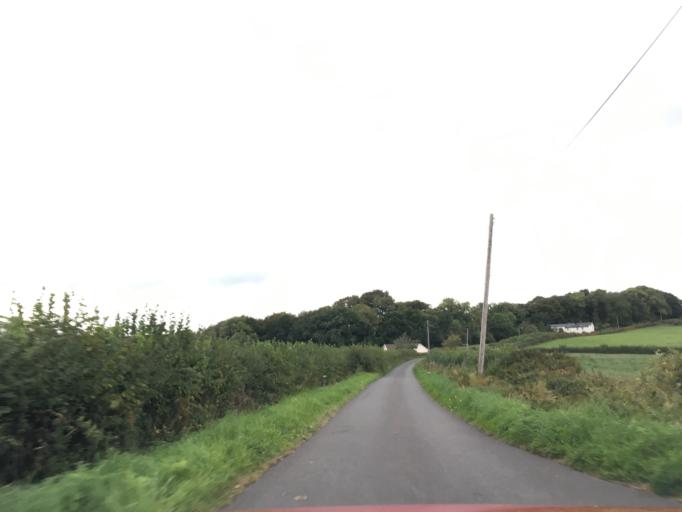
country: GB
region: Wales
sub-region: Newport
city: Caerleon
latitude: 51.6353
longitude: -2.9338
